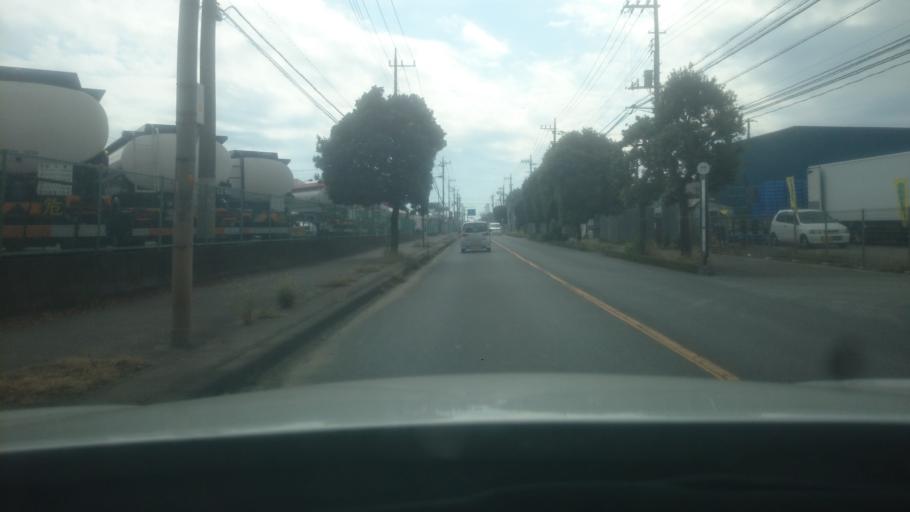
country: JP
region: Saitama
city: Oi
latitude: 35.8121
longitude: 139.5212
